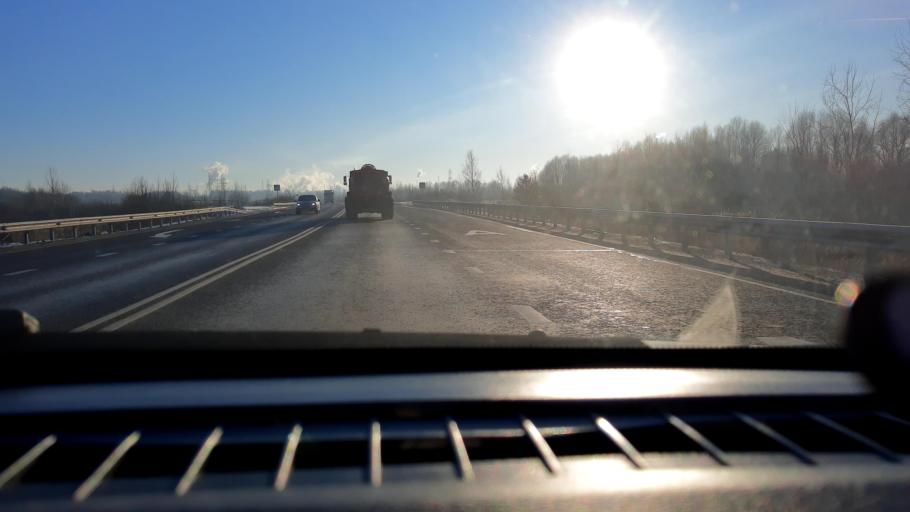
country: RU
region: Nizjnij Novgorod
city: Kstovo
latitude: 56.1384
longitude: 44.1560
